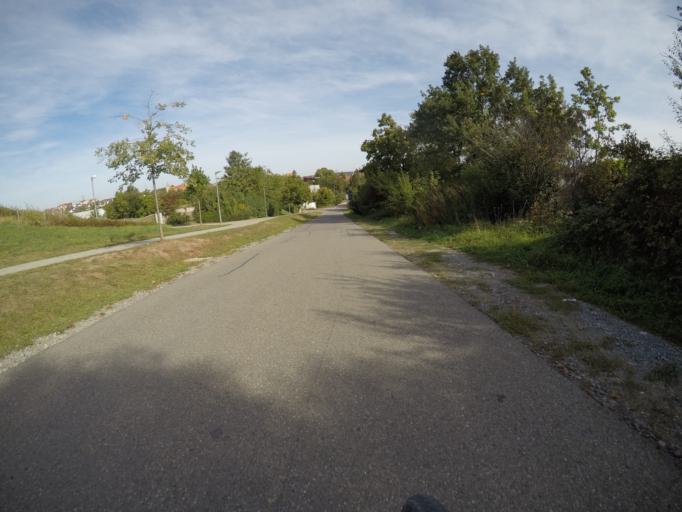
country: DE
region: Baden-Wuerttemberg
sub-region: Regierungsbezirk Stuttgart
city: Markgroningen
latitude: 48.8990
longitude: 9.0814
